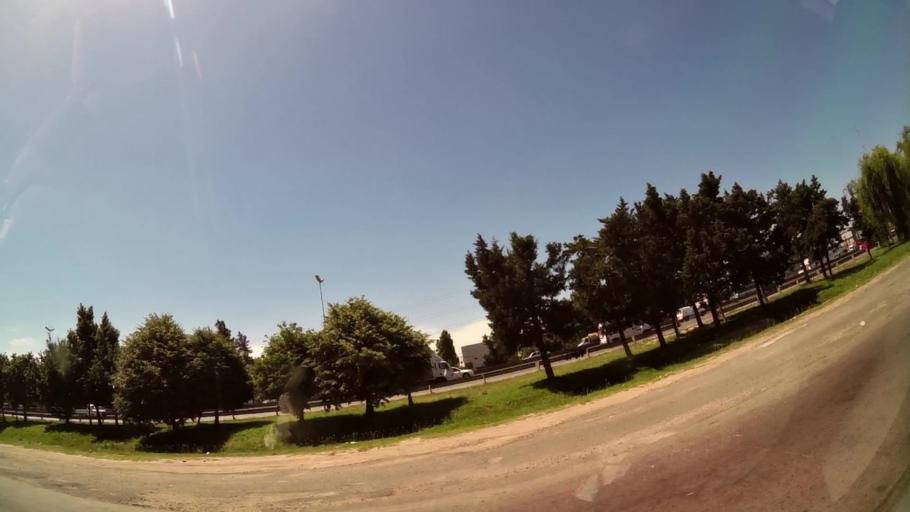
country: AR
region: Buenos Aires
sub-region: Partido de Tigre
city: Tigre
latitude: -34.4822
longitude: -58.6373
